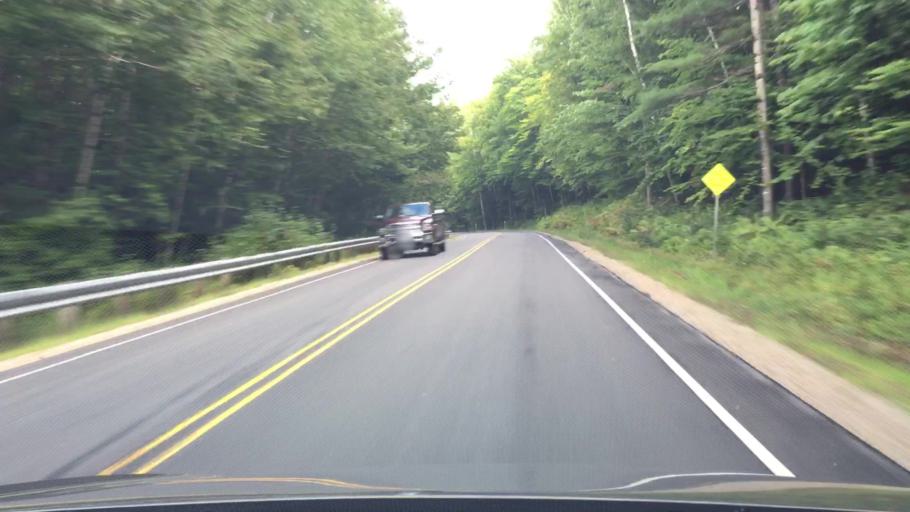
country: US
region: New Hampshire
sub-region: Carroll County
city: Conway
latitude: 43.9904
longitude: -71.1786
